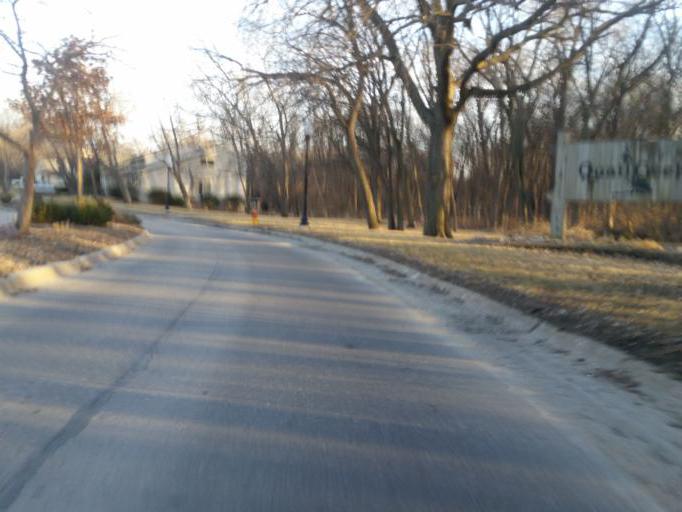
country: US
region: Nebraska
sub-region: Sarpy County
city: Offutt Air Force Base
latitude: 41.1366
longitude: -95.9745
